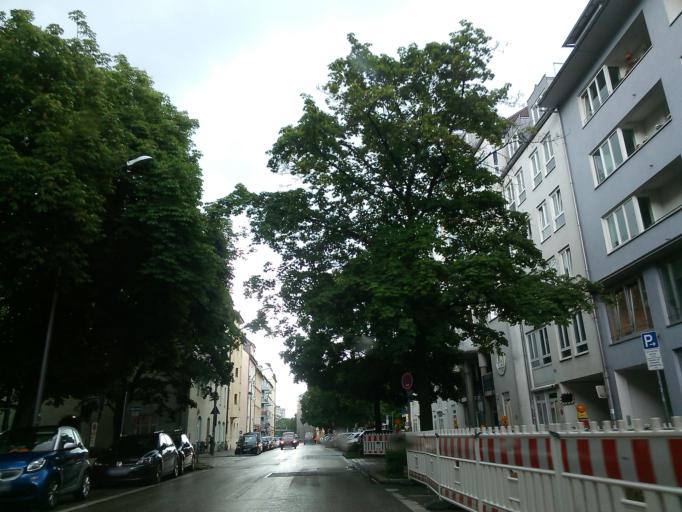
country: DE
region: Bavaria
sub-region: Upper Bavaria
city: Munich
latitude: 48.1255
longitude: 11.5956
